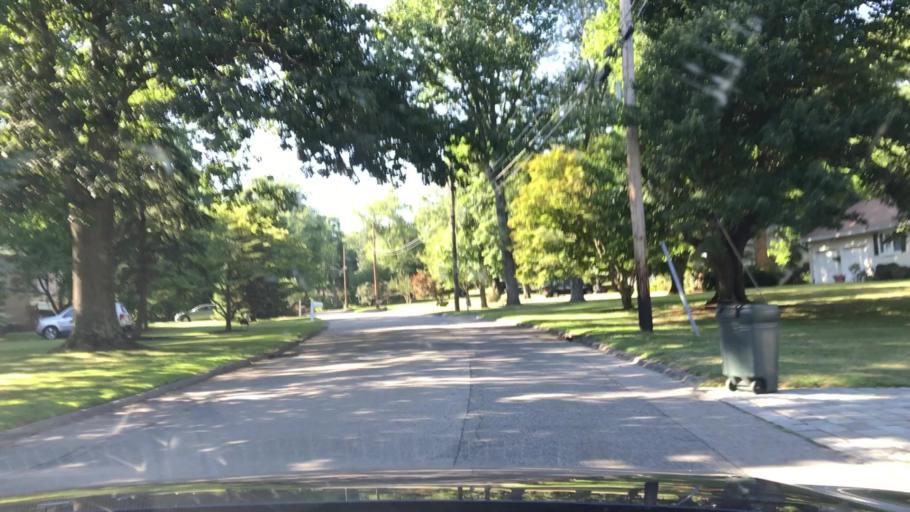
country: US
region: New York
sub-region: Westchester County
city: Thornwood
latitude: 41.1099
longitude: -73.7790
